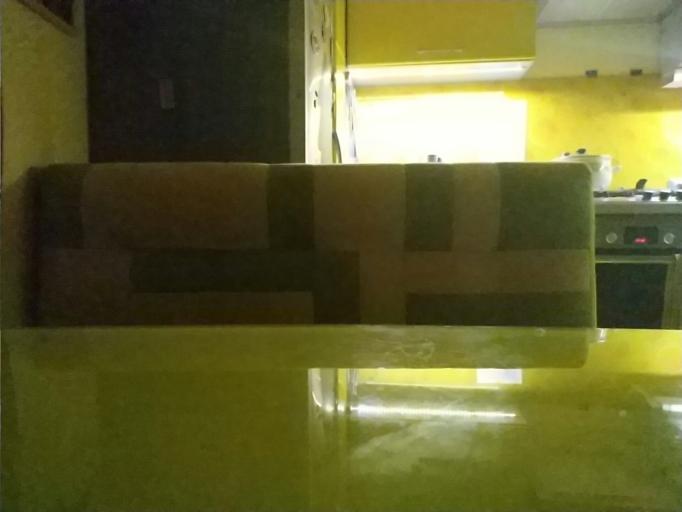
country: RU
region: Murmansk
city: Alakurtti
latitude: 66.3901
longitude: 30.2034
